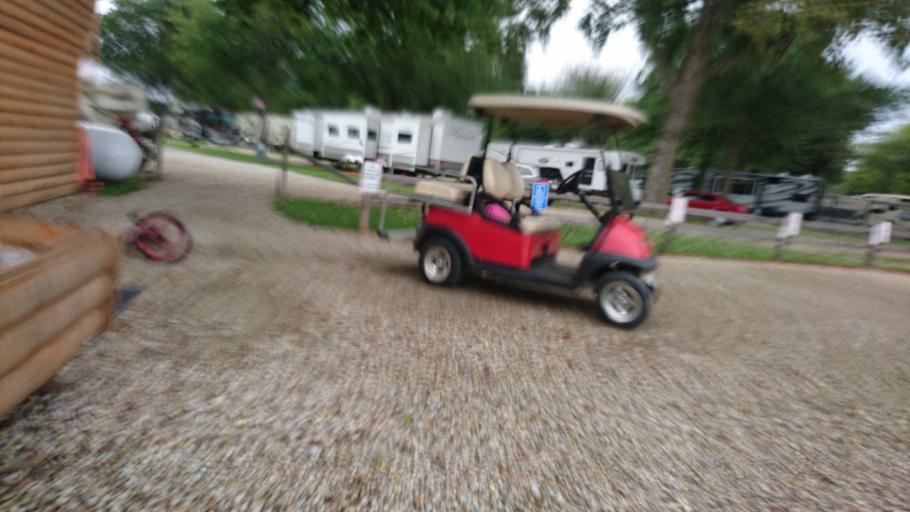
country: US
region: Illinois
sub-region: Sangamon County
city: Chatham
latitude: 39.6572
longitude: -89.6488
